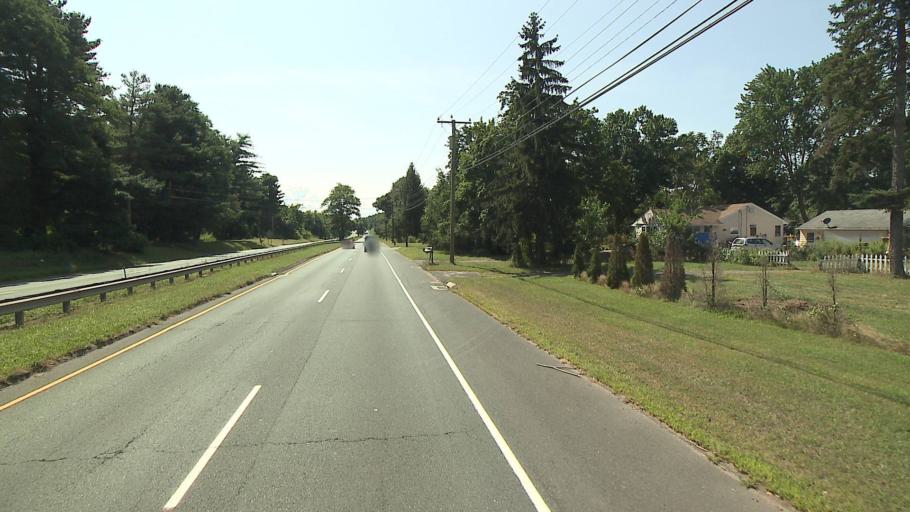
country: US
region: Connecticut
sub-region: Hartford County
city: Windsor
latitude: 41.8662
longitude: -72.6051
